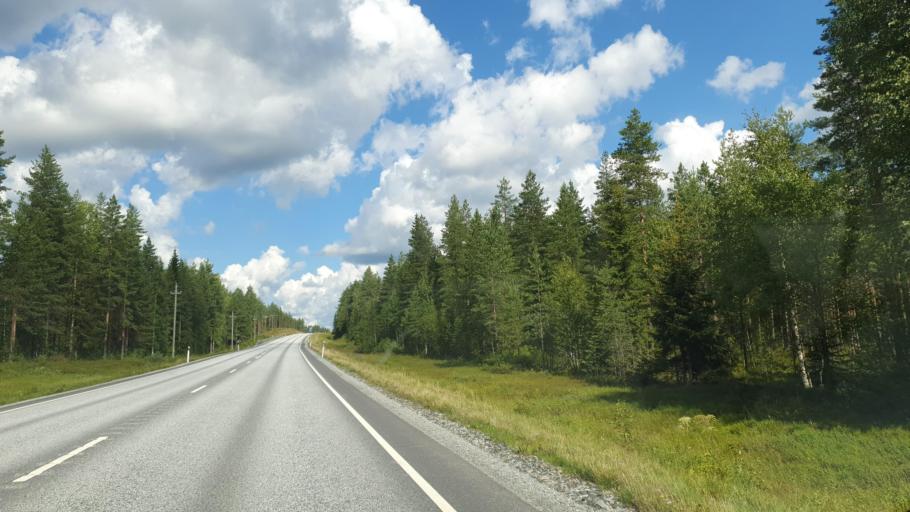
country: FI
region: Northern Savo
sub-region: Ylae-Savo
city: Sonkajaervi
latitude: 63.9437
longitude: 27.3734
